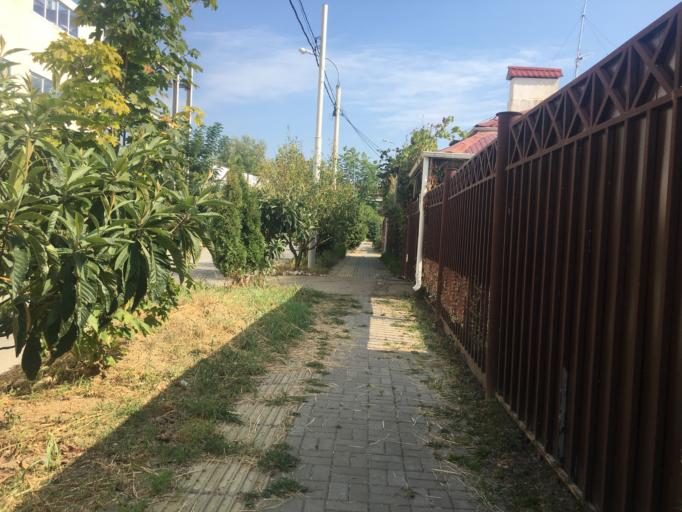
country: RU
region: Krasnodarskiy
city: Vysokoye
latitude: 43.3944
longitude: 40.0019
